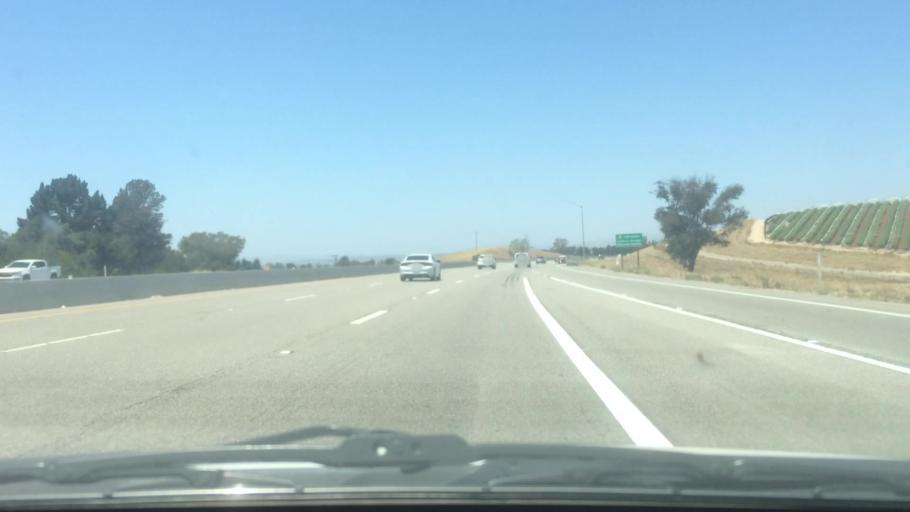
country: US
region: California
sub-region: Santa Barbara County
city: Orcutt
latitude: 34.8895
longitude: -120.4166
